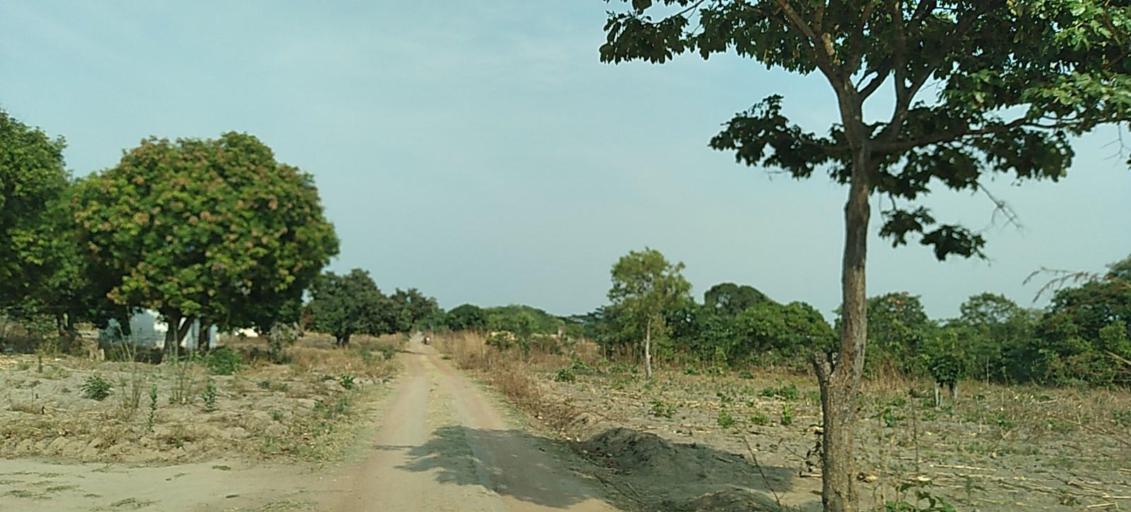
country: ZM
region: Copperbelt
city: Ndola
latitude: -13.2223
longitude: 28.6709
